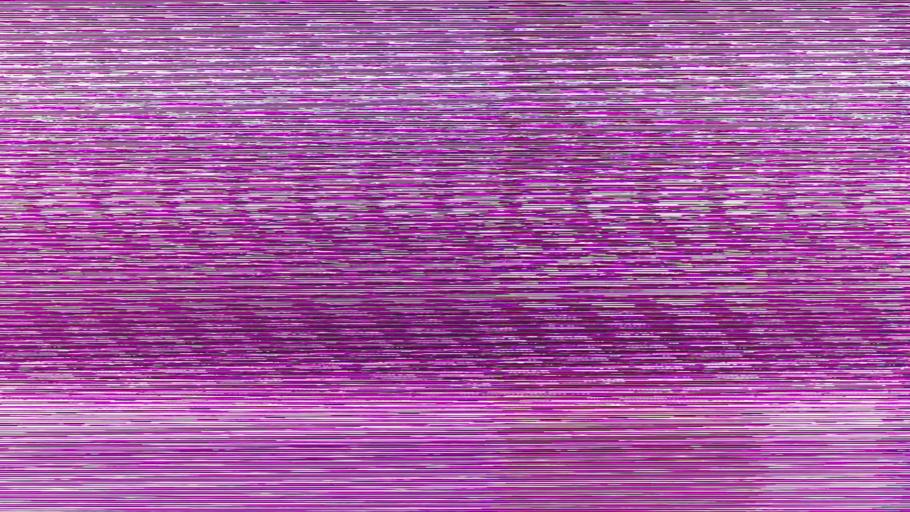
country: US
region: Michigan
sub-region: Wayne County
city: Detroit
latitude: 42.3488
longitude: -83.0236
